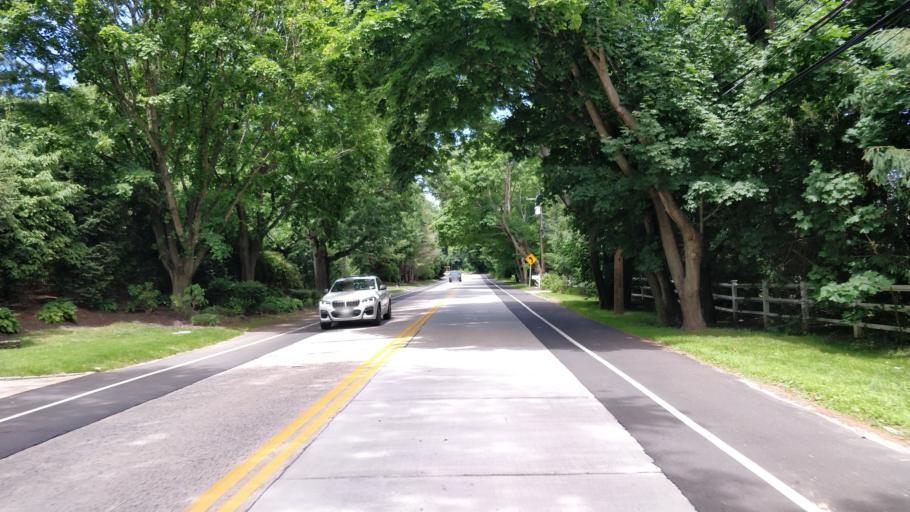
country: US
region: New York
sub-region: Nassau County
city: Laurel Hollow
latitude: 40.8435
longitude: -73.4776
